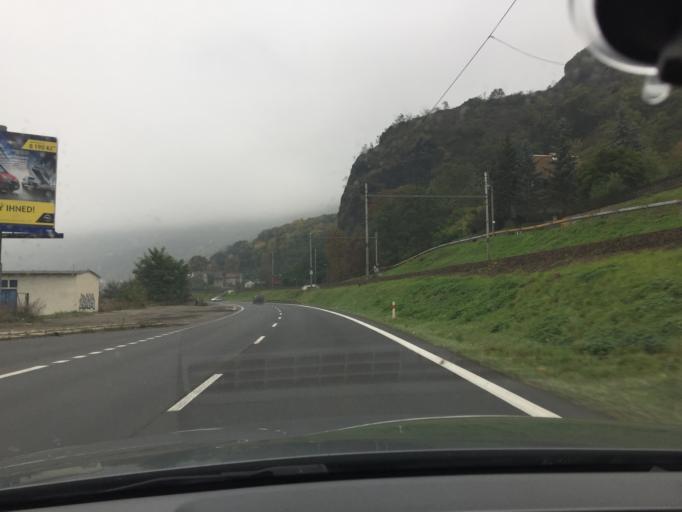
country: CZ
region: Ustecky
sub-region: Okres Usti nad Labem
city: Usti nad Labem
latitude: 50.6332
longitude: 14.0474
